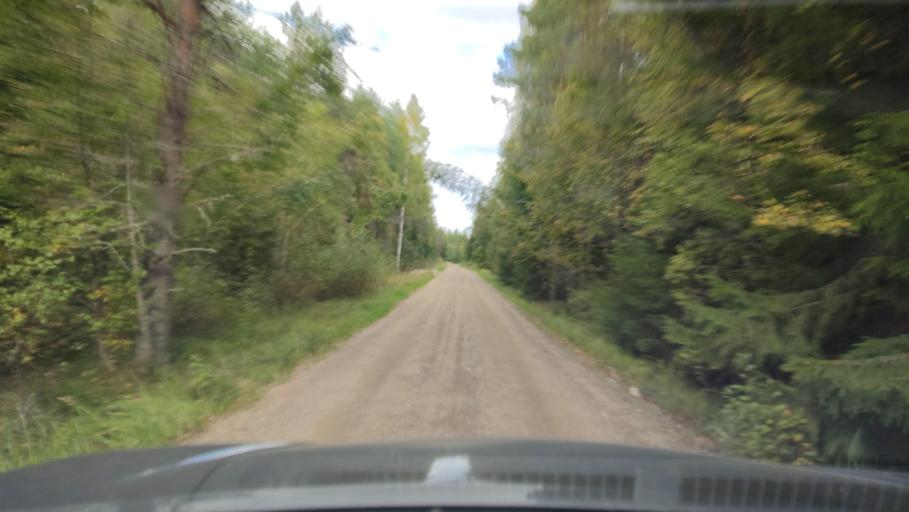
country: FI
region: Southern Ostrobothnia
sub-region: Suupohja
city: Karijoki
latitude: 62.2052
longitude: 21.6152
